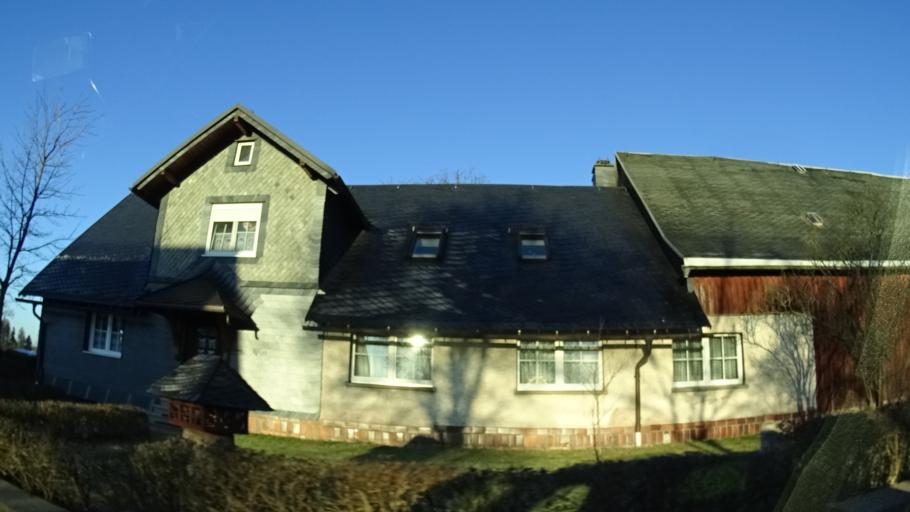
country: DE
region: Thuringia
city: Judenbach
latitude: 50.3962
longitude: 11.2210
